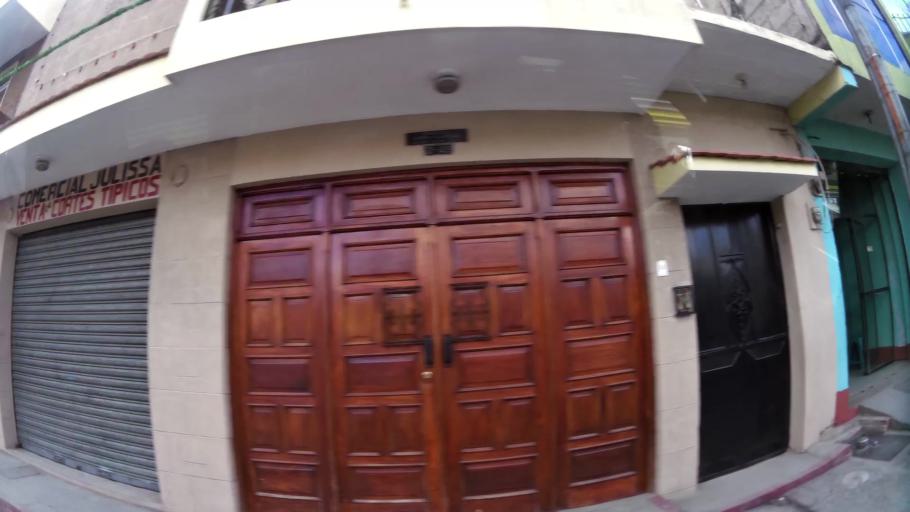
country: GT
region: Quetzaltenango
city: Salcaja
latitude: 14.8781
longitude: -91.4602
